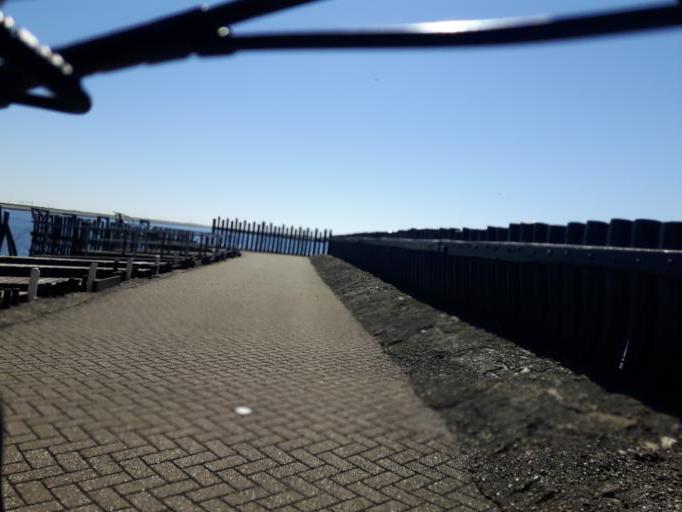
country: NL
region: Zeeland
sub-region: Gemeente Tholen
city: Tholen
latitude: 51.5232
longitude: 4.1541
